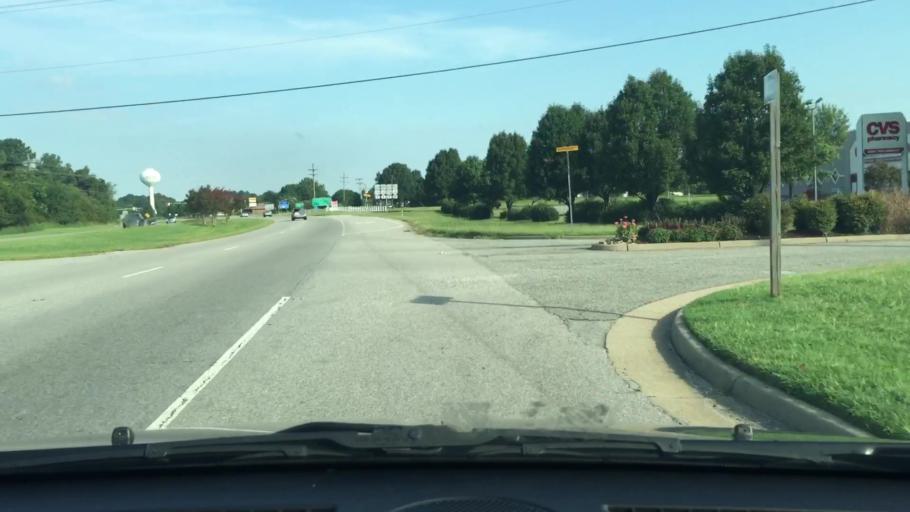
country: US
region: Virginia
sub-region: Isle of Wight County
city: Smithfield
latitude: 36.9586
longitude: -76.6032
